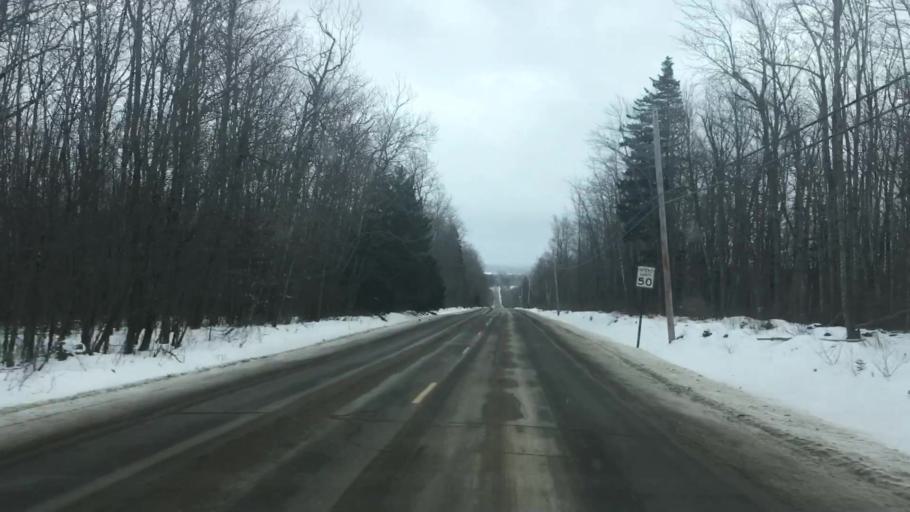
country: US
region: Maine
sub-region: Washington County
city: East Machias
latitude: 44.9758
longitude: -67.4509
